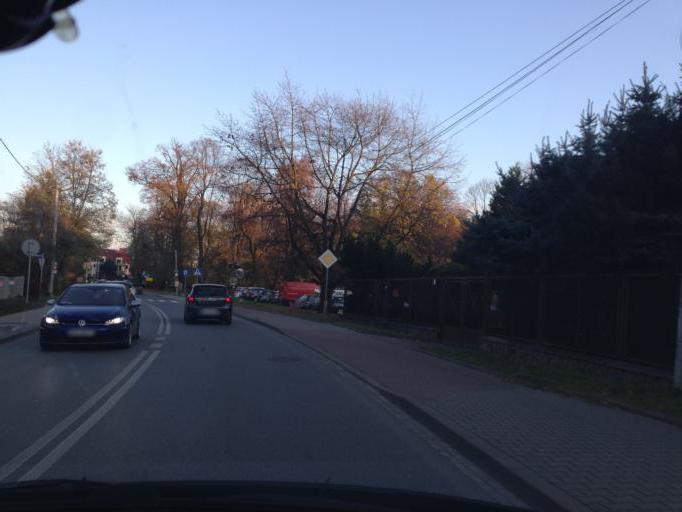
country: PL
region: Lesser Poland Voivodeship
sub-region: Powiat krakowski
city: Rzaska
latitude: 50.0666
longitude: 19.8708
